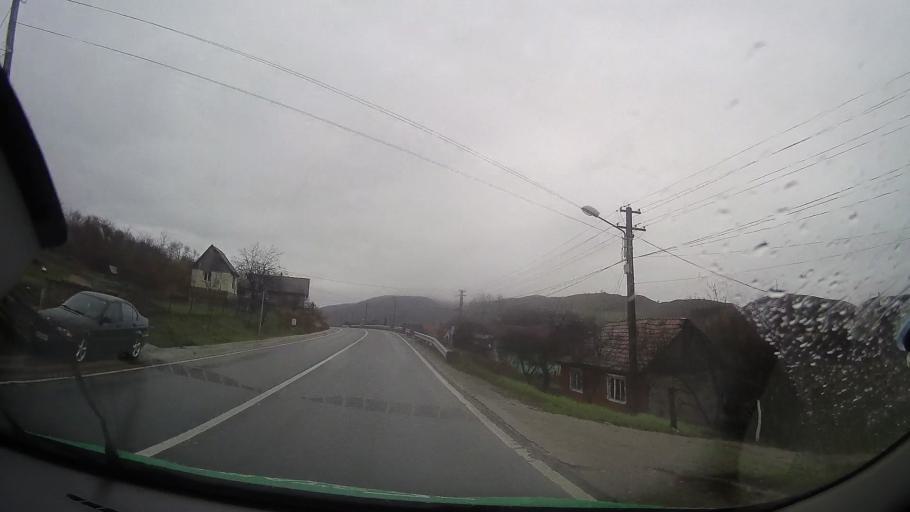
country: RO
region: Bistrita-Nasaud
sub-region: Comuna Galatii Bistritei
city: Galatii Bistritei
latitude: 46.9518
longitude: 24.4491
